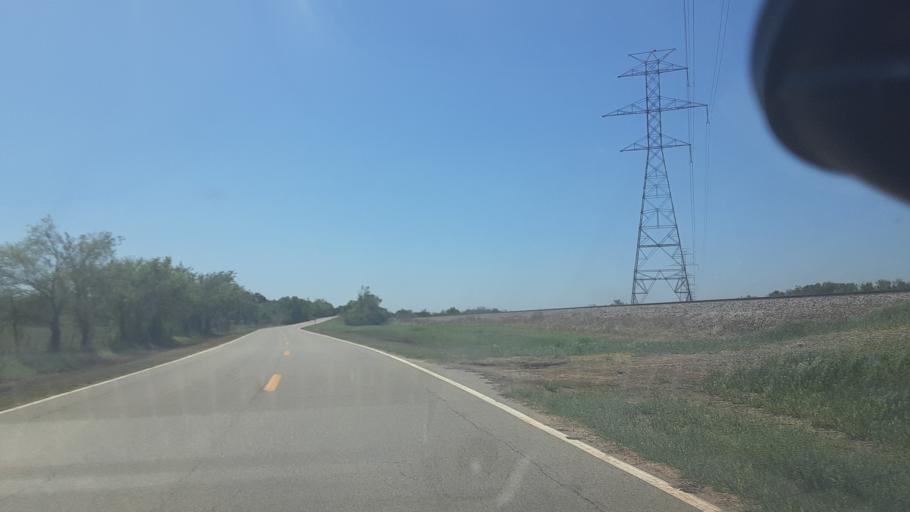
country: US
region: Oklahoma
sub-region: Logan County
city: Langston
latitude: 36.0941
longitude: -97.3953
